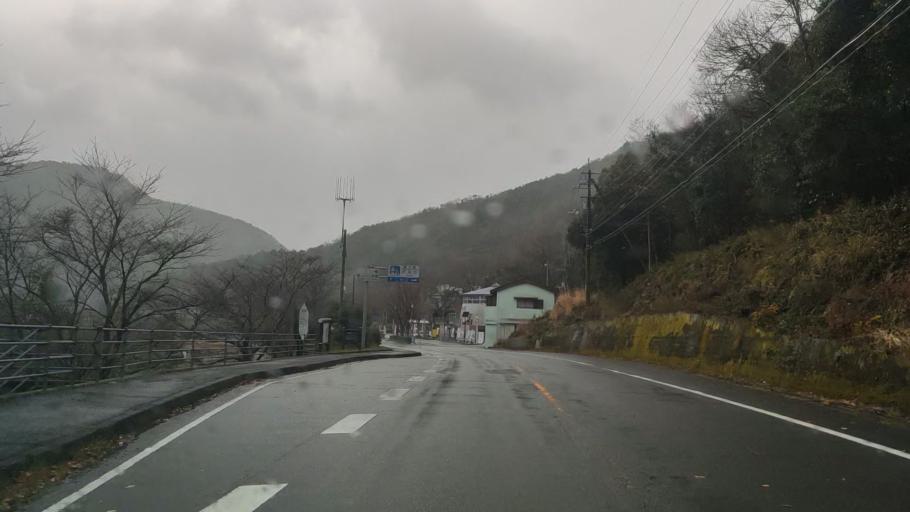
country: JP
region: Tokushima
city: Kamojimacho-jogejima
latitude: 34.1522
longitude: 134.3527
